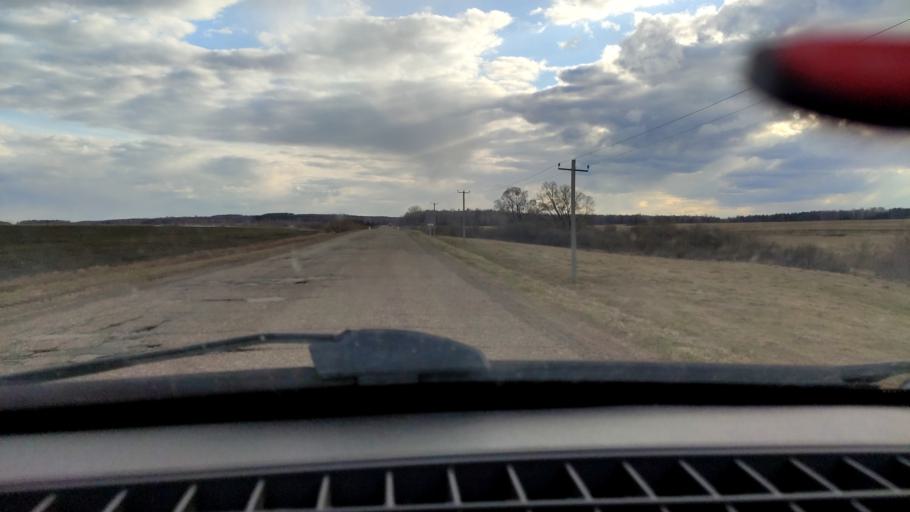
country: RU
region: Bashkortostan
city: Karmaskaly
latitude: 54.3299
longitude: 55.9915
